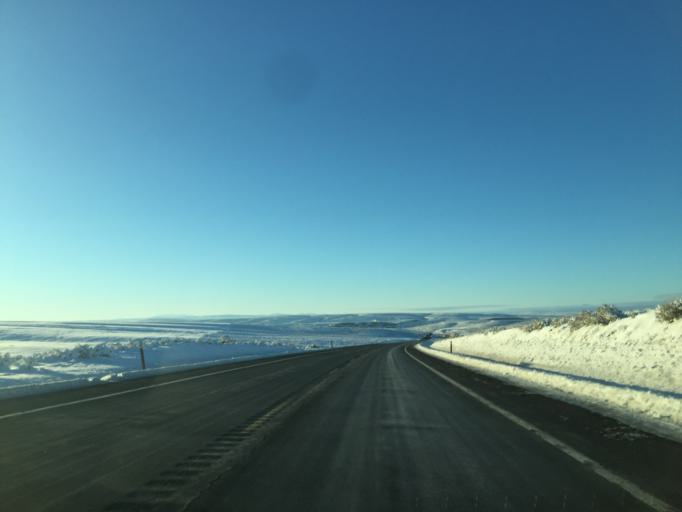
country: US
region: Washington
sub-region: Grant County
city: Soap Lake
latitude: 47.5997
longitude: -119.6098
